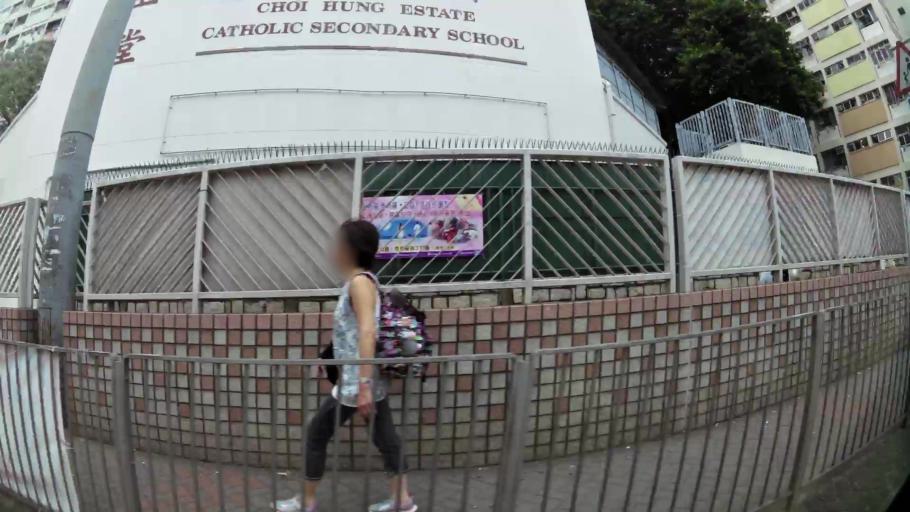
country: HK
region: Wong Tai Sin
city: Wong Tai Sin
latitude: 22.3356
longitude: 114.2074
